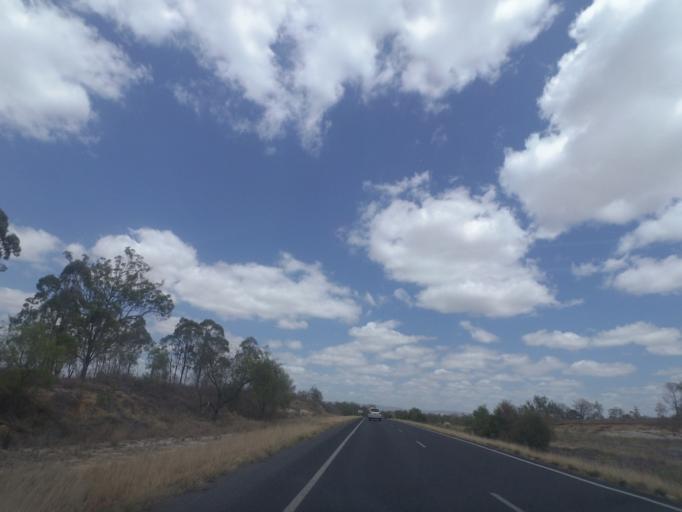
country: AU
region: Queensland
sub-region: Lockyer Valley
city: Gatton
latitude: -27.5521
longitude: 152.1562
